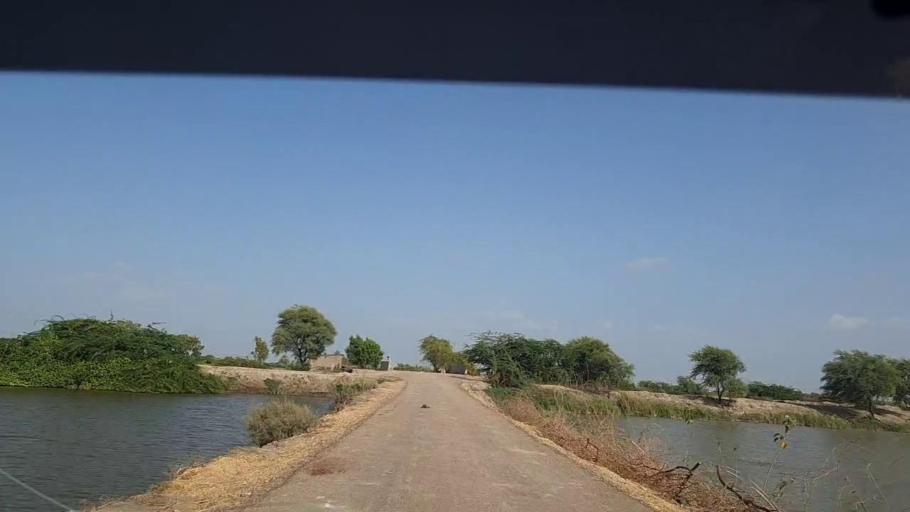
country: PK
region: Sindh
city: Kadhan
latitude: 24.4638
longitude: 68.8462
